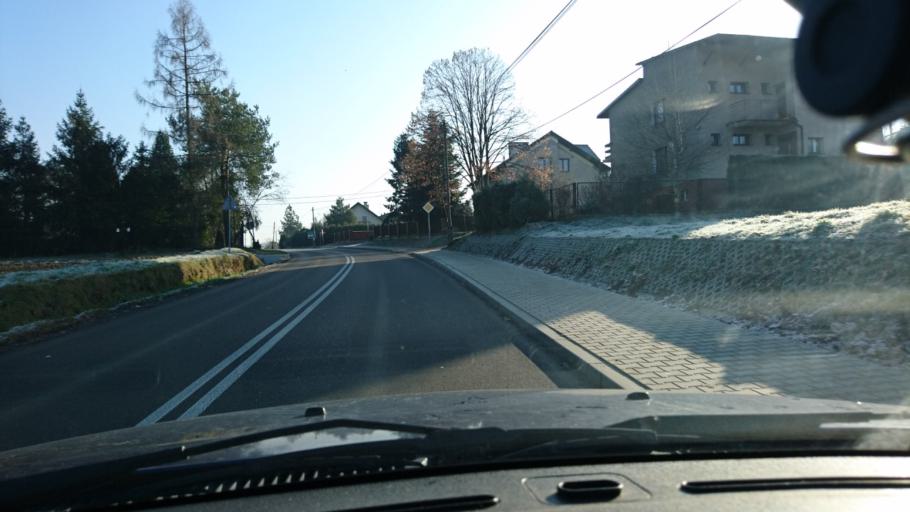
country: PL
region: Silesian Voivodeship
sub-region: Powiat bielski
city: Bestwina
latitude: 49.8958
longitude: 19.0716
